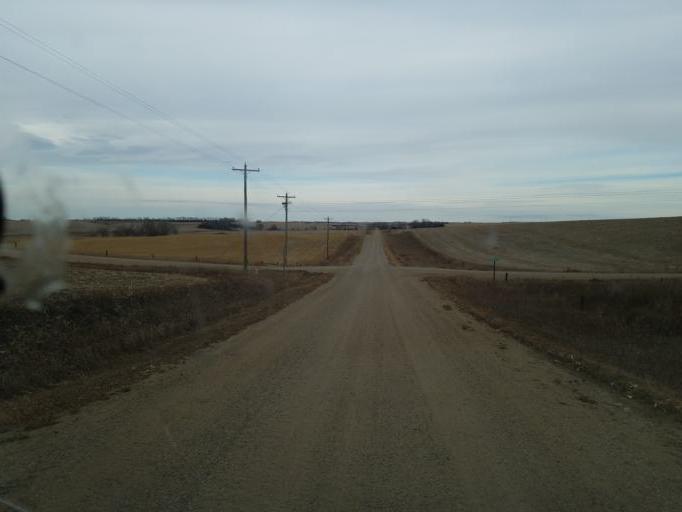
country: US
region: Nebraska
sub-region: Knox County
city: Bloomfield
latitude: 42.5825
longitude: -97.7205
